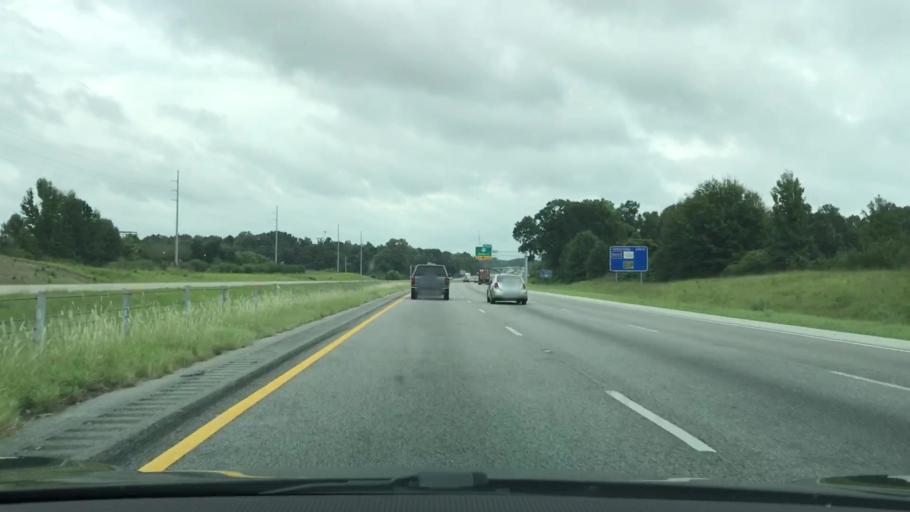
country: US
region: Alabama
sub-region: Lee County
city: Auburn
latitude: 32.5527
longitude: -85.5204
